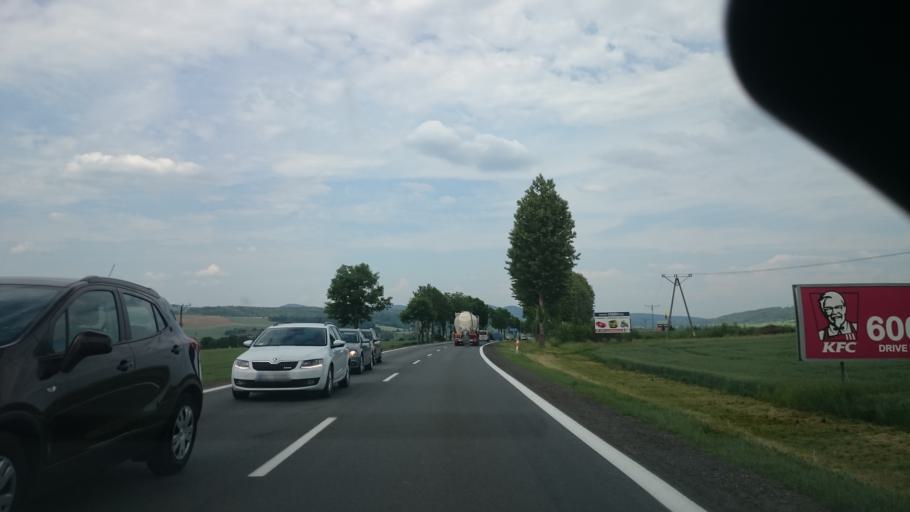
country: PL
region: Lower Silesian Voivodeship
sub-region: Powiat klodzki
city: Klodzko
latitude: 50.4495
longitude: 16.6306
